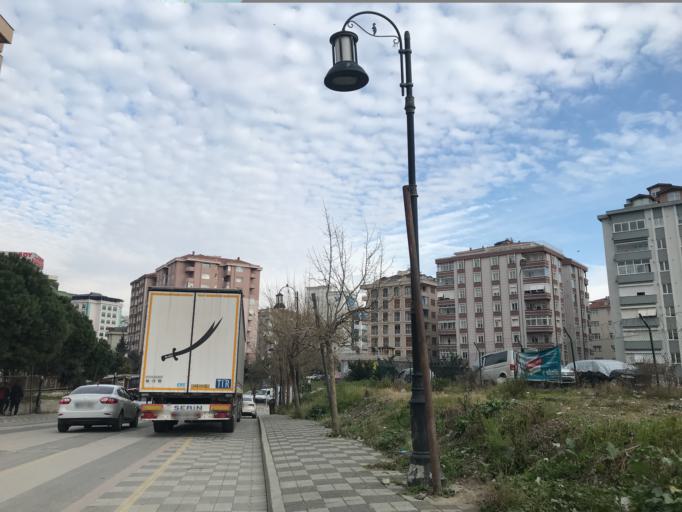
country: TR
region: Istanbul
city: Maltepe
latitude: 40.9328
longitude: 29.1330
